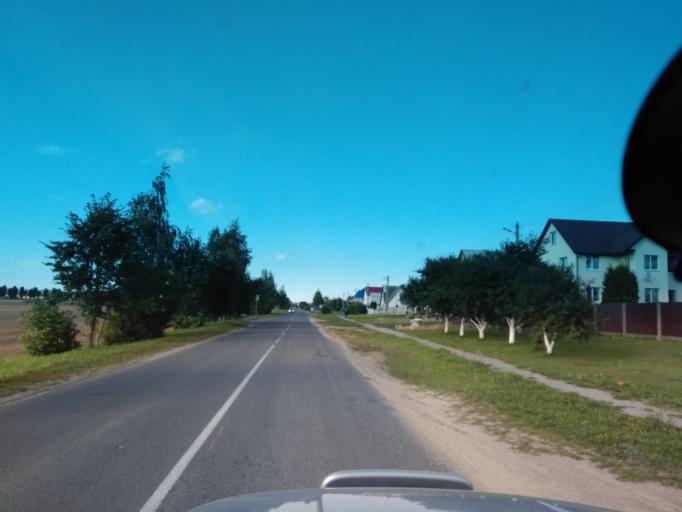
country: BY
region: Minsk
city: Dzyarzhynsk
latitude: 53.6712
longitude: 27.1117
